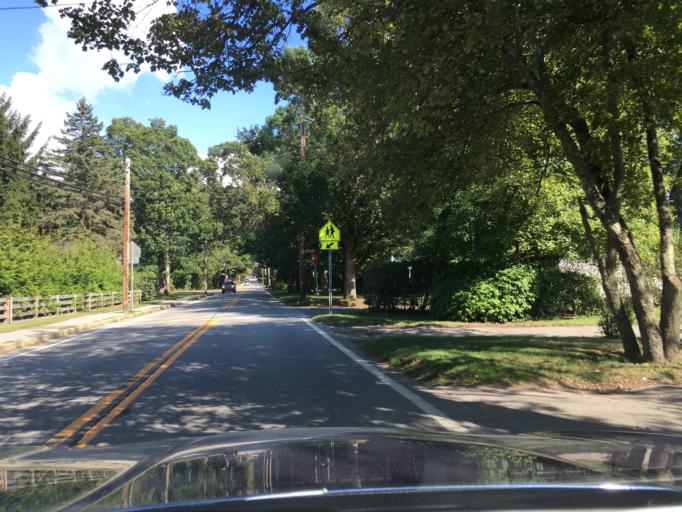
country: US
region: Rhode Island
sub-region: Bristol County
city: Barrington
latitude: 41.7287
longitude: -71.3098
